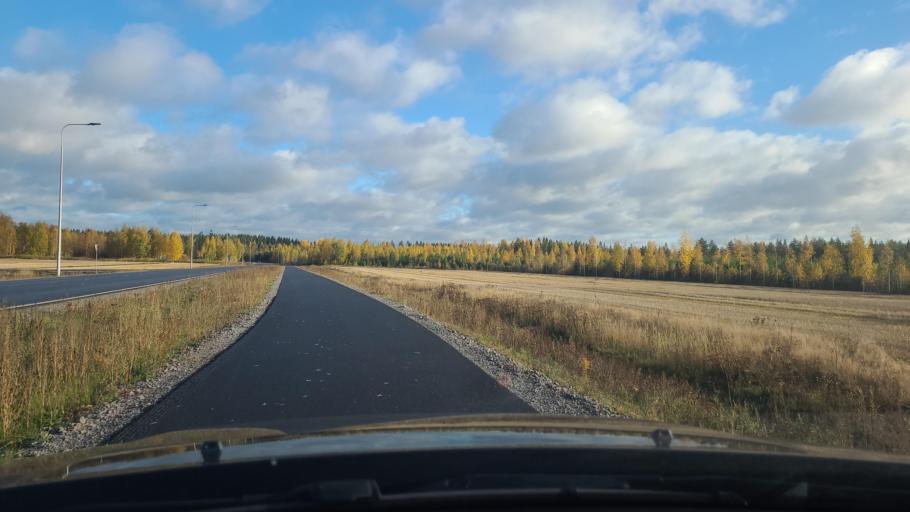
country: FI
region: Southern Savonia
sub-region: Pieksaemaeki
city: Juva
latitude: 61.8930
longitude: 27.8019
